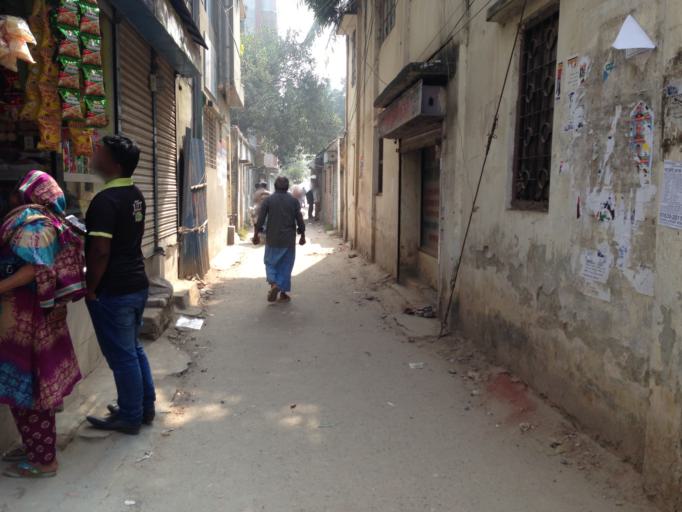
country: BD
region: Dhaka
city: Azimpur
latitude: 23.8026
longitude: 90.3510
